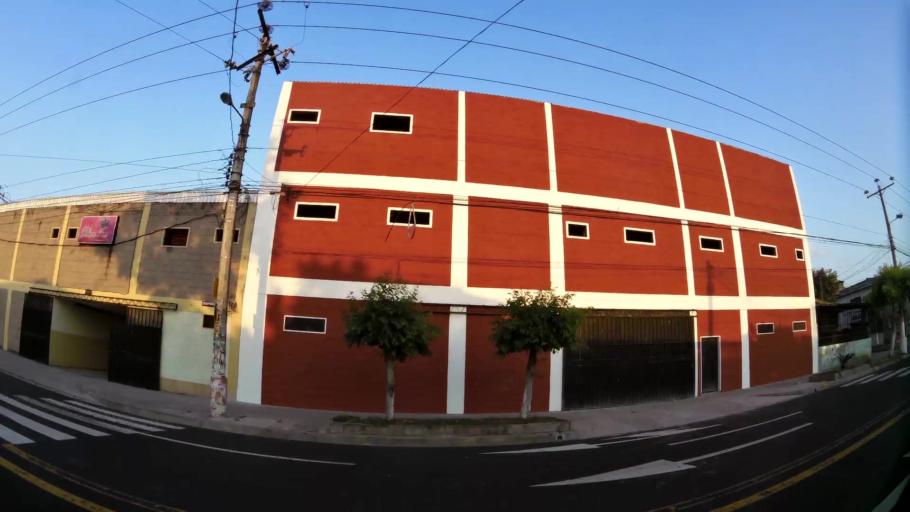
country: SV
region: San Salvador
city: Delgado
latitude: 13.7148
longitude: -89.1821
